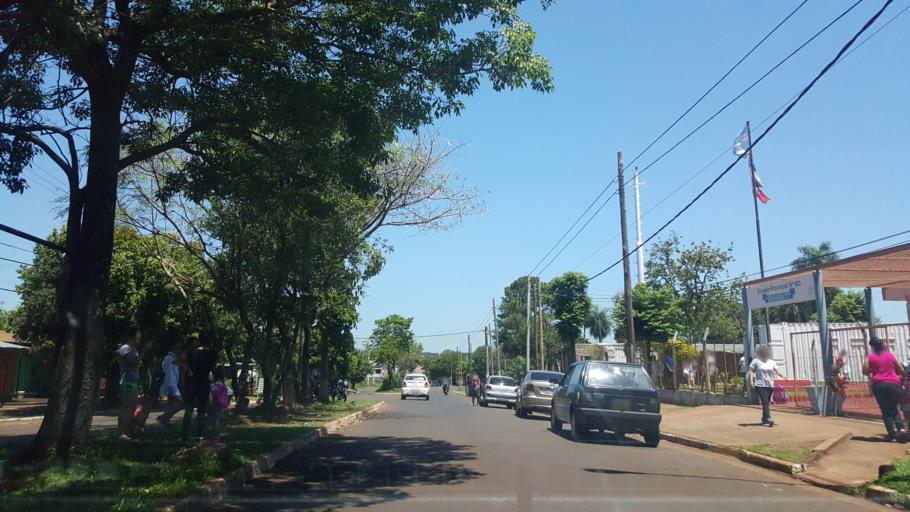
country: AR
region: Misiones
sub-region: Departamento de Capital
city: Posadas
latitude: -27.3800
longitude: -55.9260
